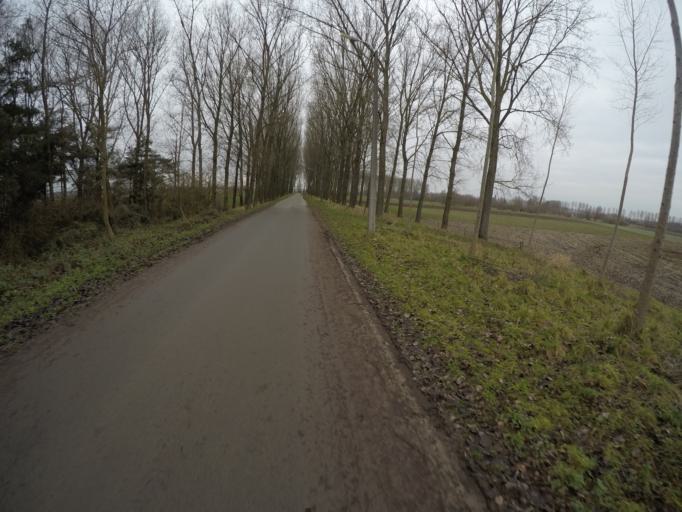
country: BE
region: Flanders
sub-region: Provincie Oost-Vlaanderen
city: Sint-Gillis-Waas
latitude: 51.2354
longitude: 4.1308
